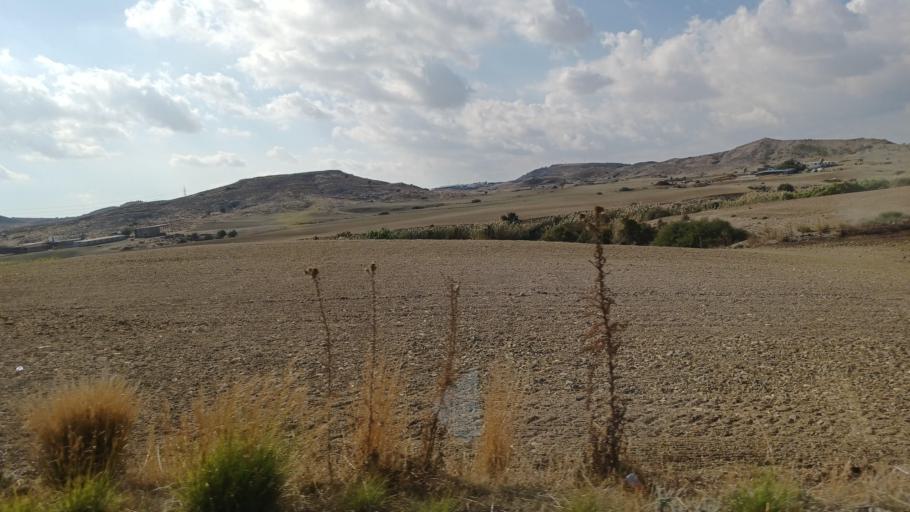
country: CY
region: Larnaka
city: Voroklini
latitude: 35.0120
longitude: 33.6413
